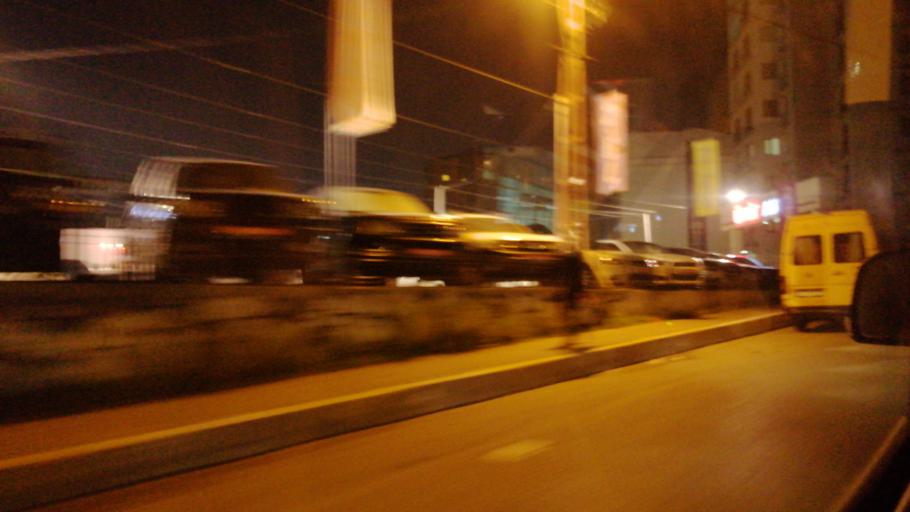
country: TR
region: Istanbul
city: Umraniye
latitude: 41.0176
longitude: 29.1285
